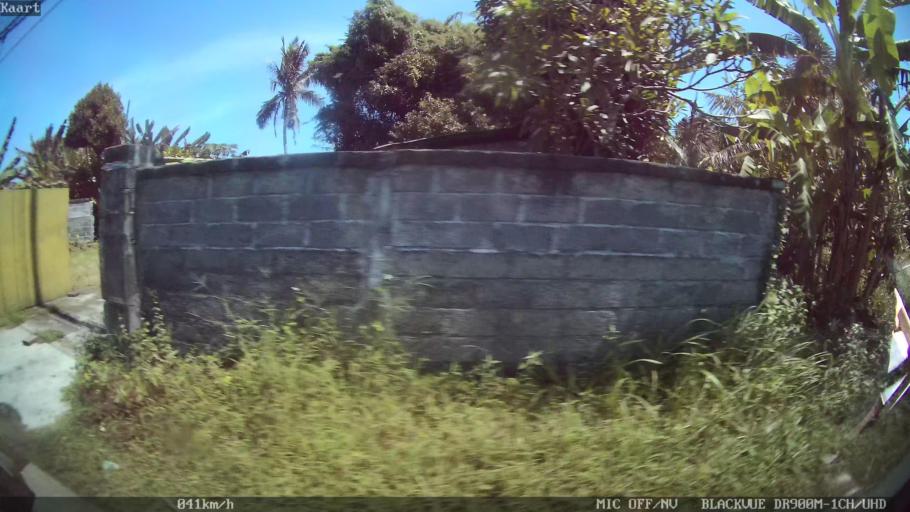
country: ID
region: Bali
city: Klungkung
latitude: -8.5682
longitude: 115.3474
